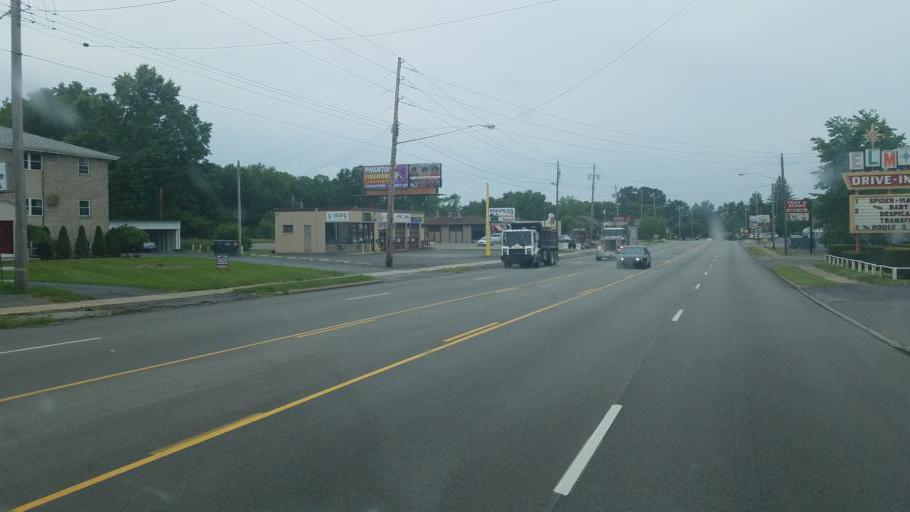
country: US
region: Ohio
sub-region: Trumbull County
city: Morgandale
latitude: 41.2526
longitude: -80.7945
